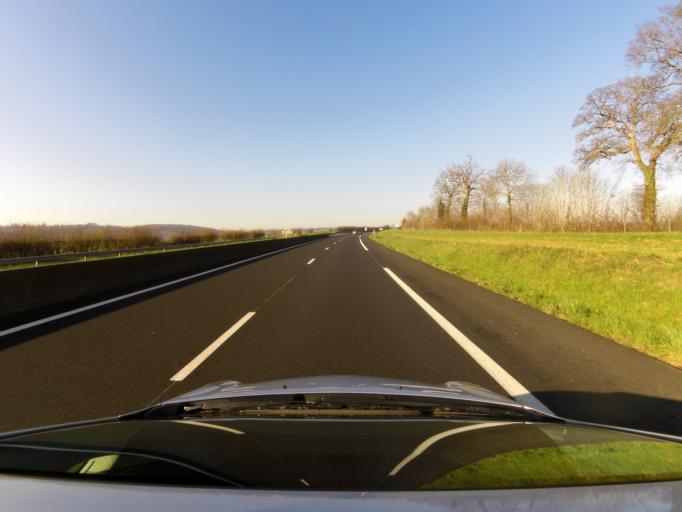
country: FR
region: Lower Normandy
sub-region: Departement du Calvados
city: Villers-Bocage
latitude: 49.0553
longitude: -0.7011
